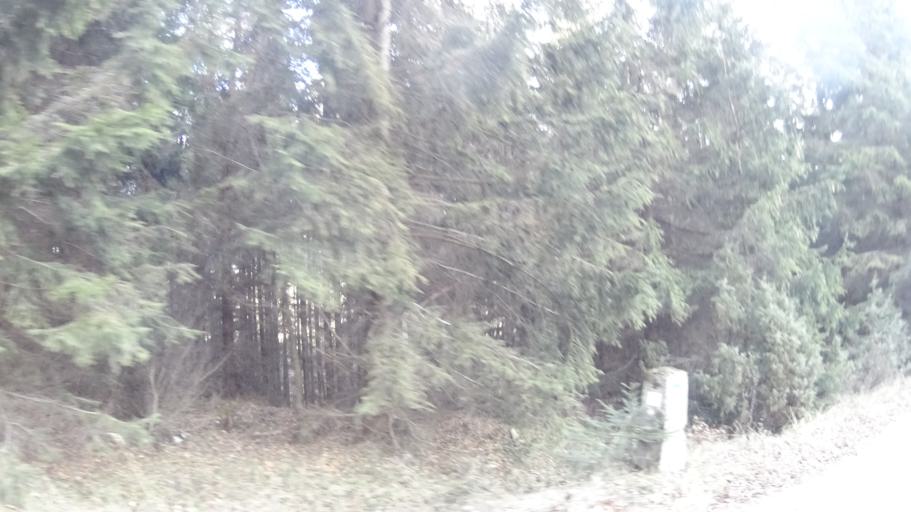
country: HU
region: Heves
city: Szilvasvarad
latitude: 48.0712
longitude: 20.4693
